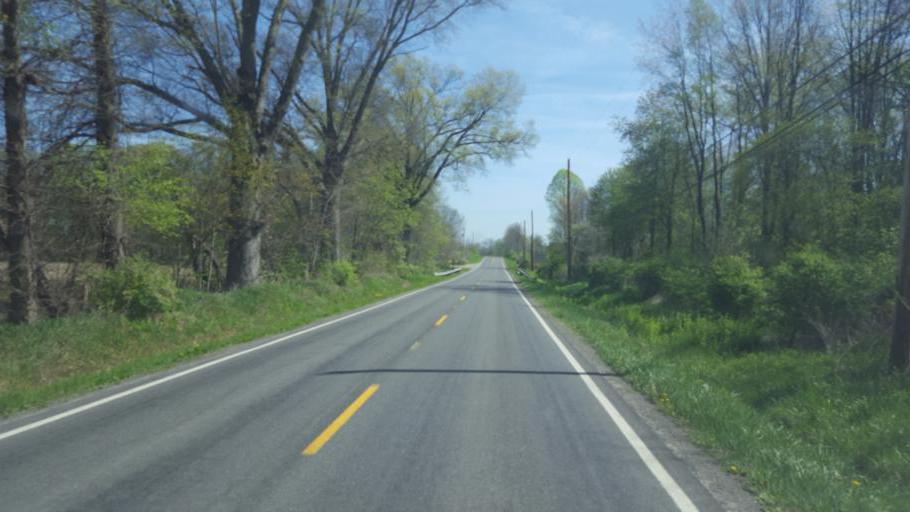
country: US
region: Ohio
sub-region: Medina County
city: Lodi
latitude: 41.0230
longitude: -82.0360
